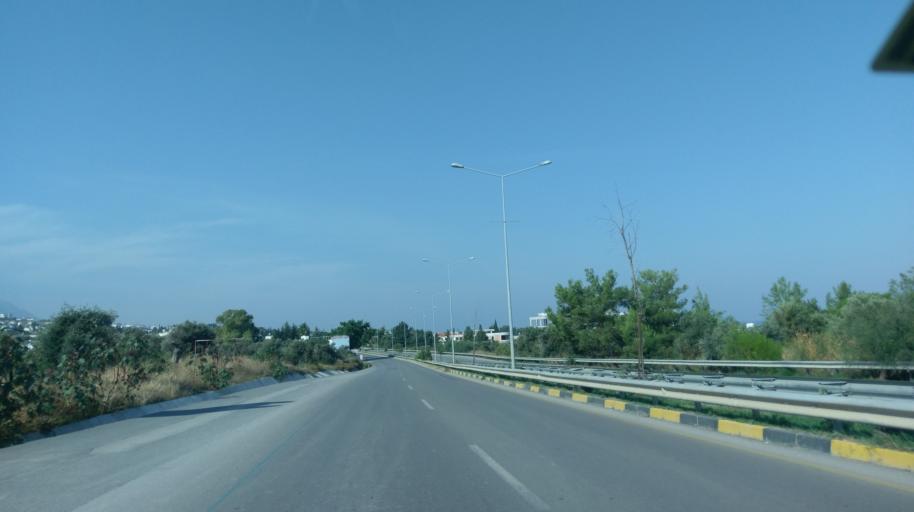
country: CY
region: Keryneia
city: Kyrenia
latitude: 35.3328
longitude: 33.2687
